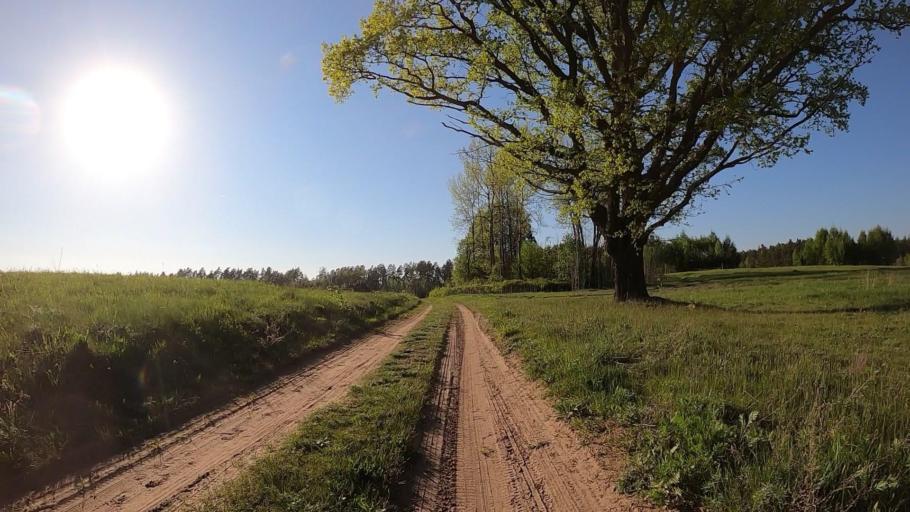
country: LV
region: Baldone
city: Baldone
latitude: 56.7726
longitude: 24.3278
